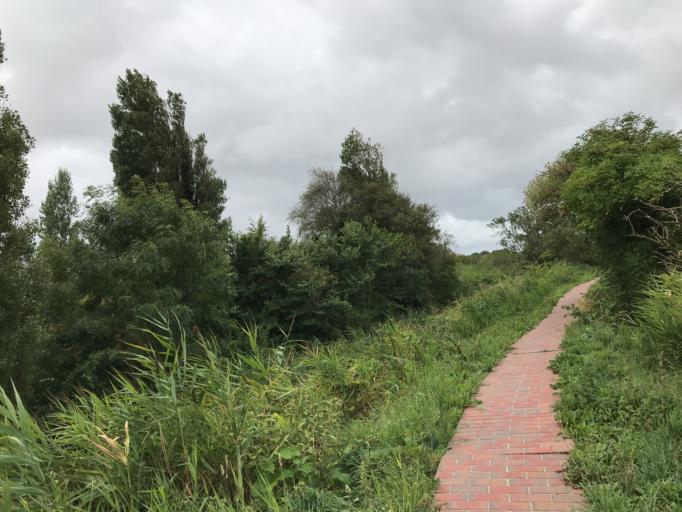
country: DE
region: Lower Saxony
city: Borkum
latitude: 53.5854
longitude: 6.6847
